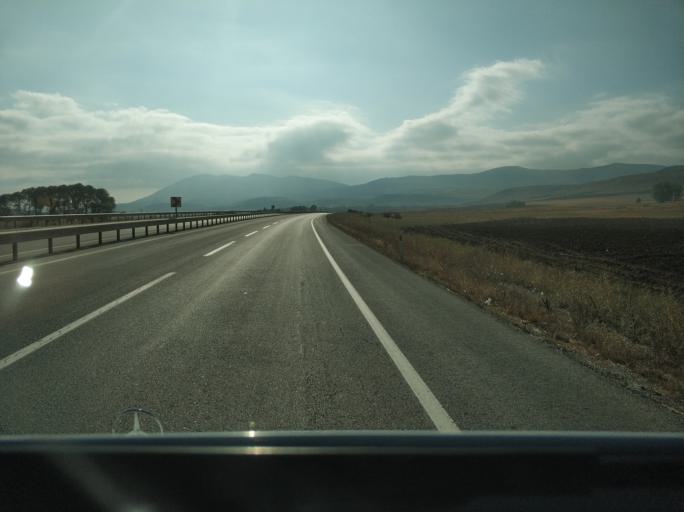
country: TR
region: Sivas
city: Yildizeli
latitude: 39.8509
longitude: 36.5070
